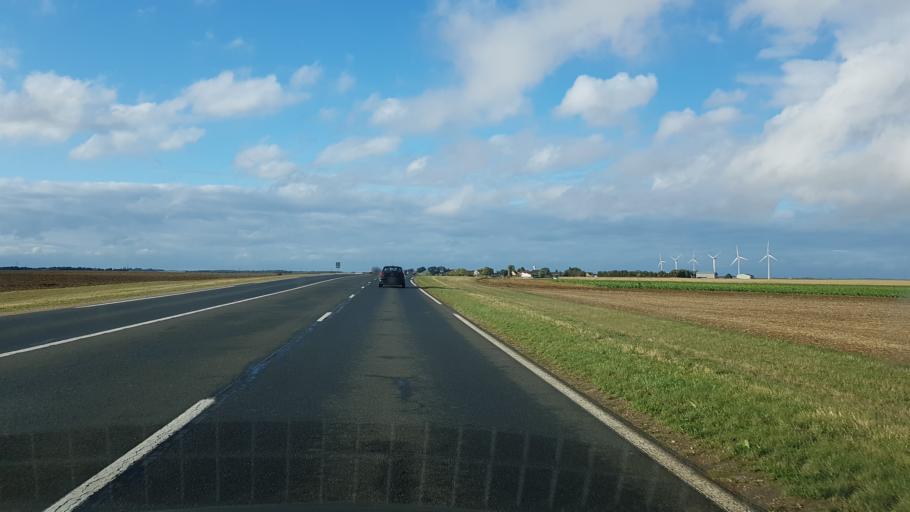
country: FR
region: Centre
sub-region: Departement du Loiret
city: Sermaises
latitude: 48.2506
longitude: 2.2171
